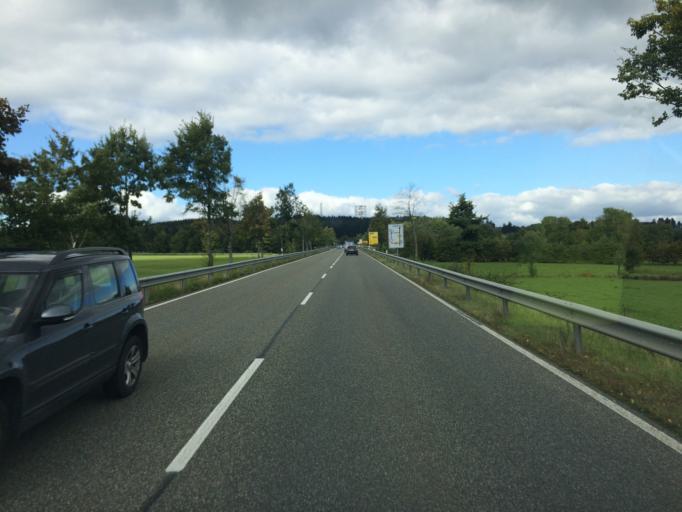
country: DE
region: Rheinland-Pfalz
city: Bretthausen
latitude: 50.6599
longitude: 8.0590
